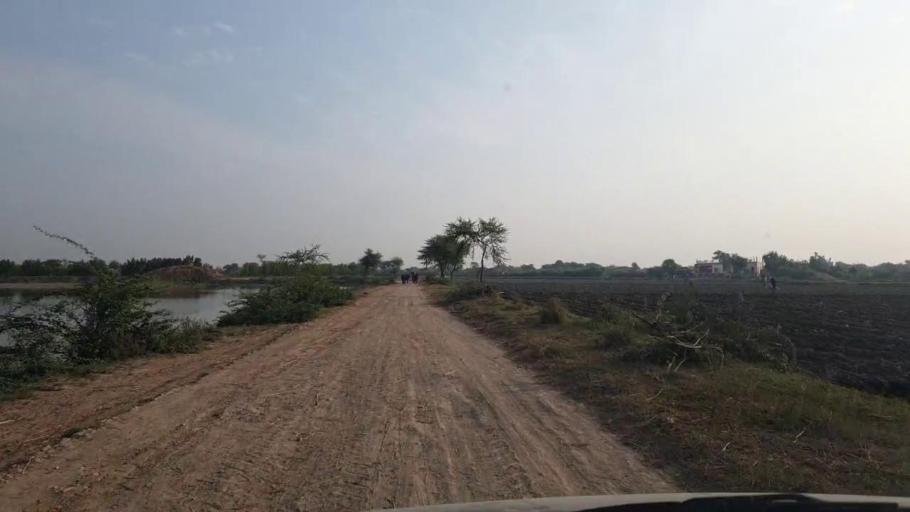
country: PK
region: Sindh
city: Tando Bago
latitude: 24.8020
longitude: 68.8808
